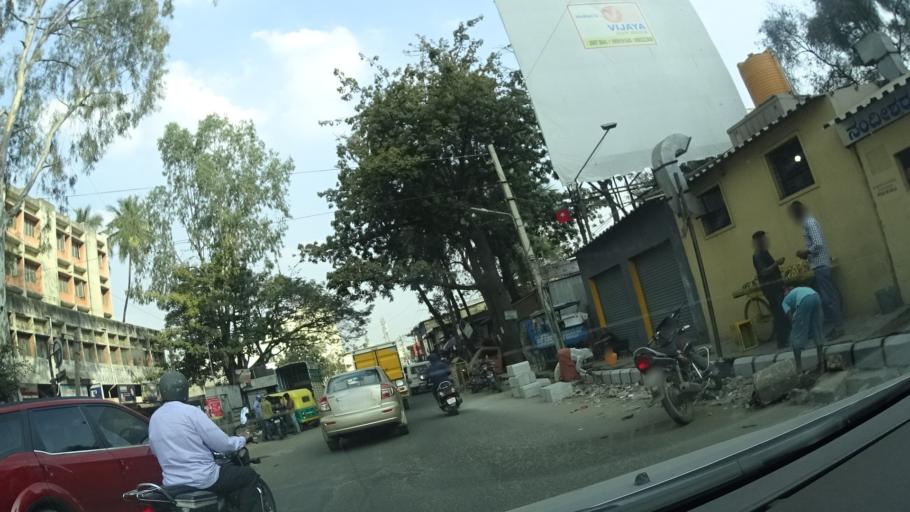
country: IN
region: Karnataka
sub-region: Bangalore Urban
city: Bangalore
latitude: 12.9555
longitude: 77.5859
